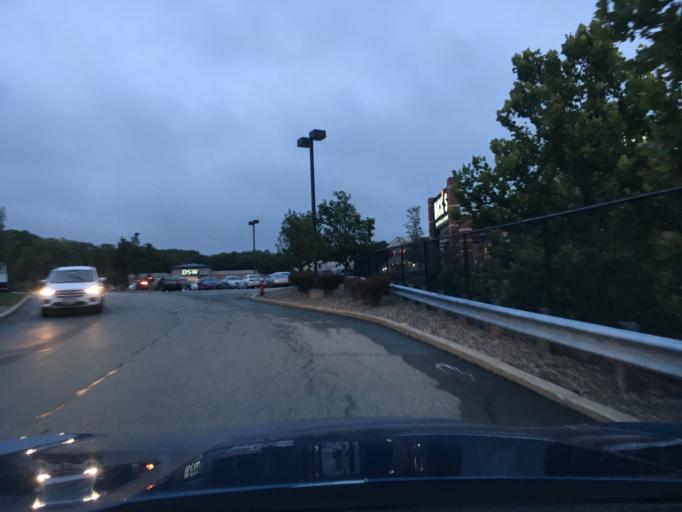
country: US
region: Rhode Island
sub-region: Kent County
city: West Warwick
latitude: 41.7020
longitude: -71.4938
